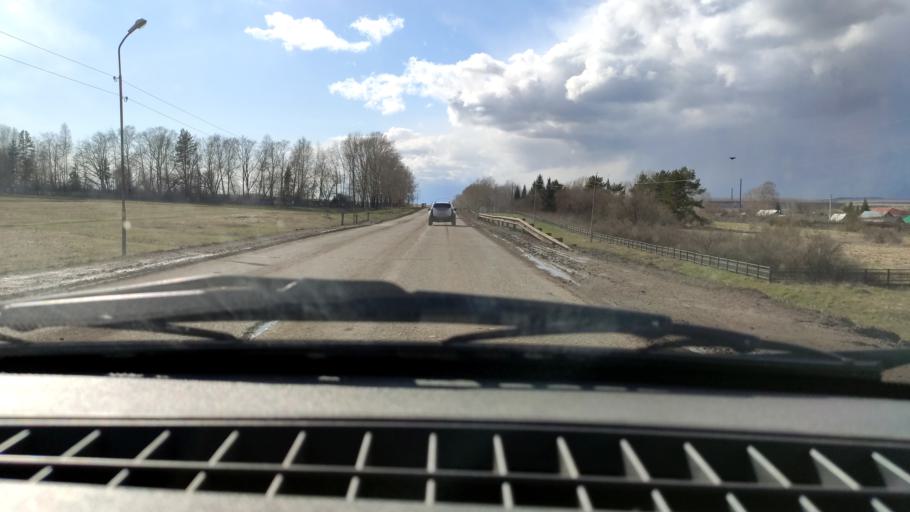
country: RU
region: Bashkortostan
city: Chekmagush
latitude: 55.1175
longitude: 54.8182
